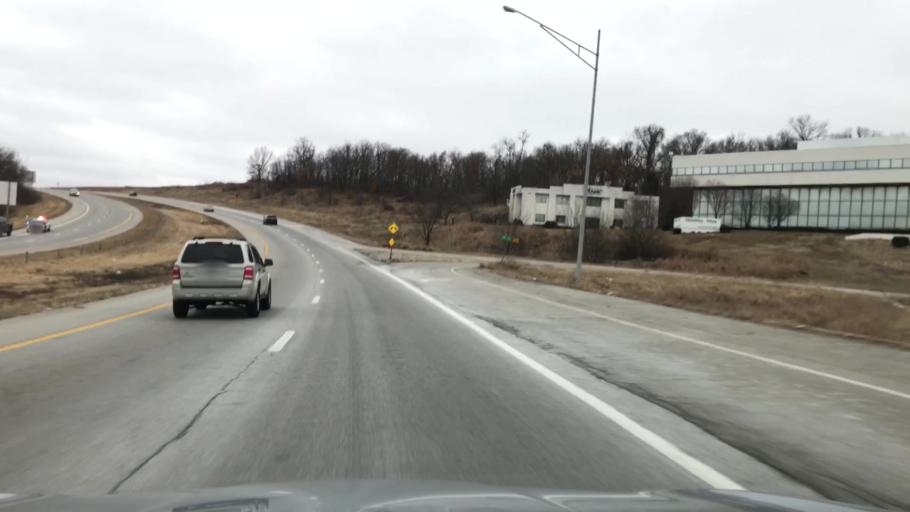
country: US
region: Missouri
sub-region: Jackson County
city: East Independence
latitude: 39.0564
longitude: -94.3668
